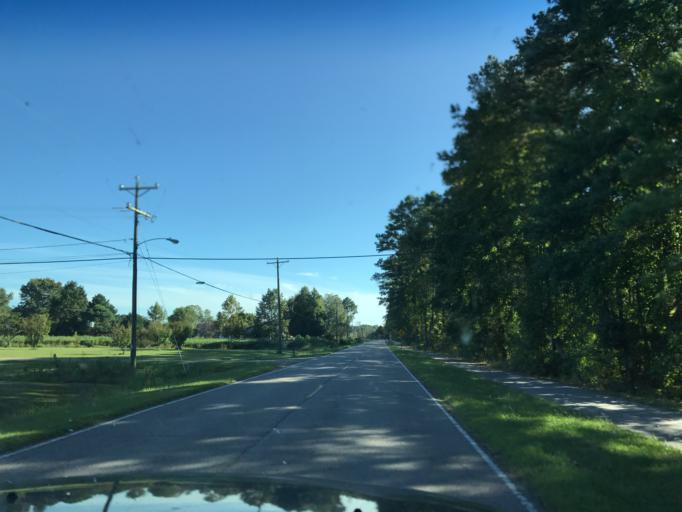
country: US
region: Virginia
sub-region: City of Portsmouth
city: Portsmouth Heights
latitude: 36.6988
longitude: -76.3567
